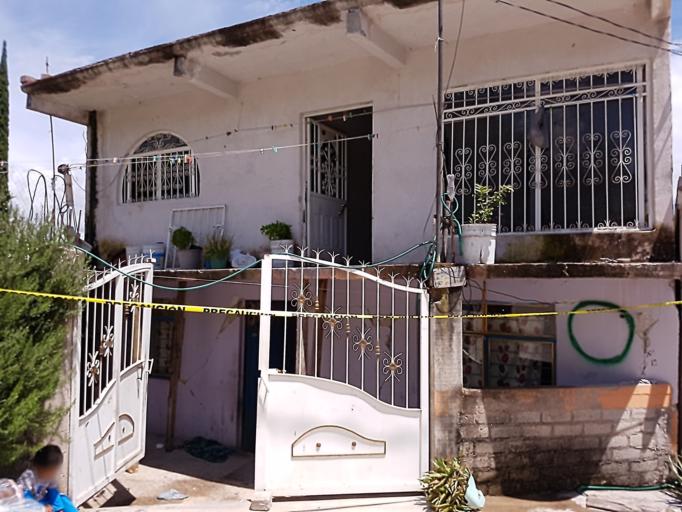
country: MX
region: Oaxaca
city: Ciudad de Huajuapam de Leon
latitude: 17.8055
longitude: -97.7954
